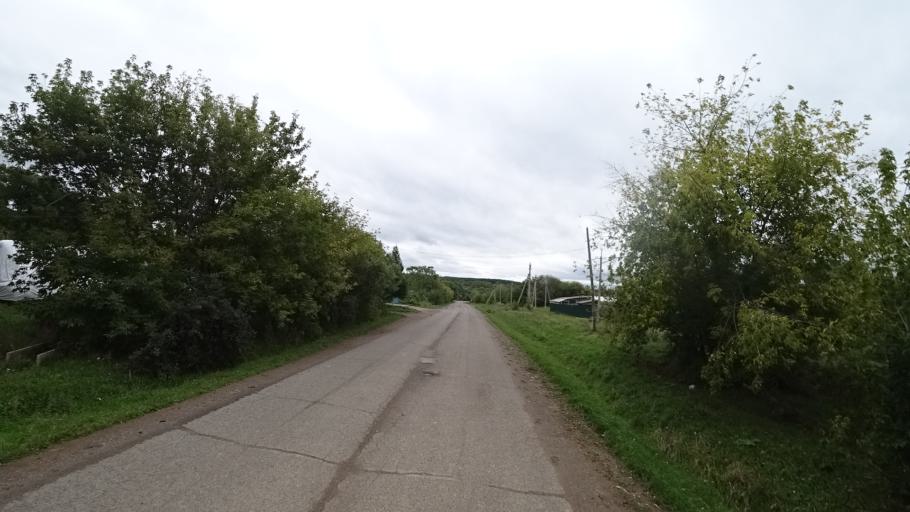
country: RU
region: Primorskiy
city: Chernigovka
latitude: 44.4634
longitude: 132.5906
